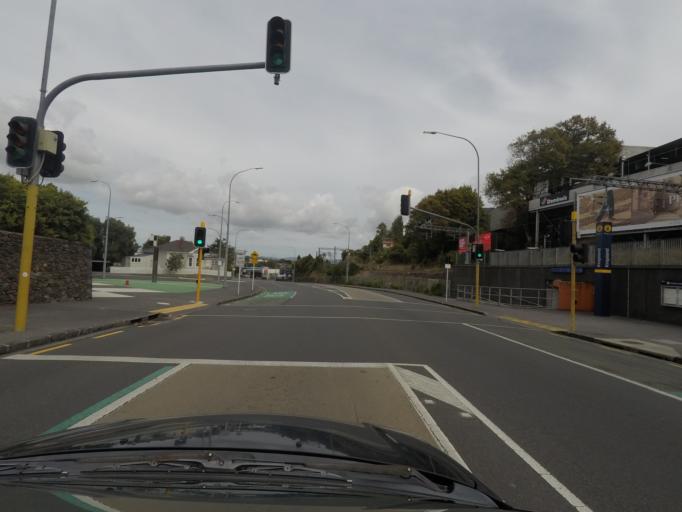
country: NZ
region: Auckland
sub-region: Auckland
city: Auckland
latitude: -36.8730
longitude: 174.7438
